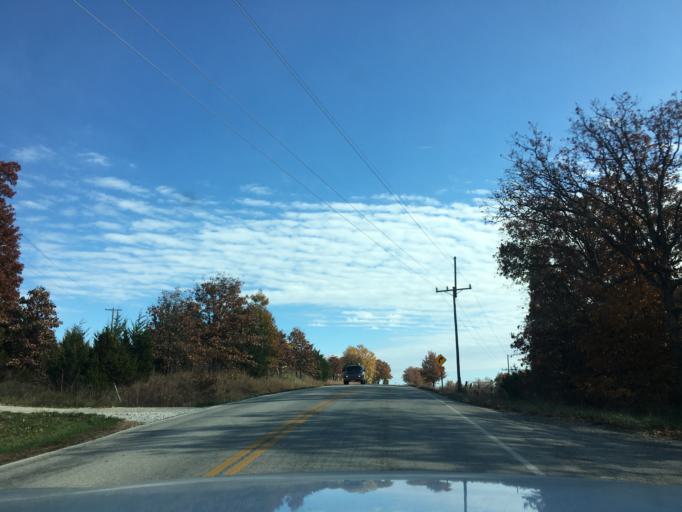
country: US
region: Missouri
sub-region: Maries County
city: Belle
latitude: 38.3244
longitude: -91.7583
